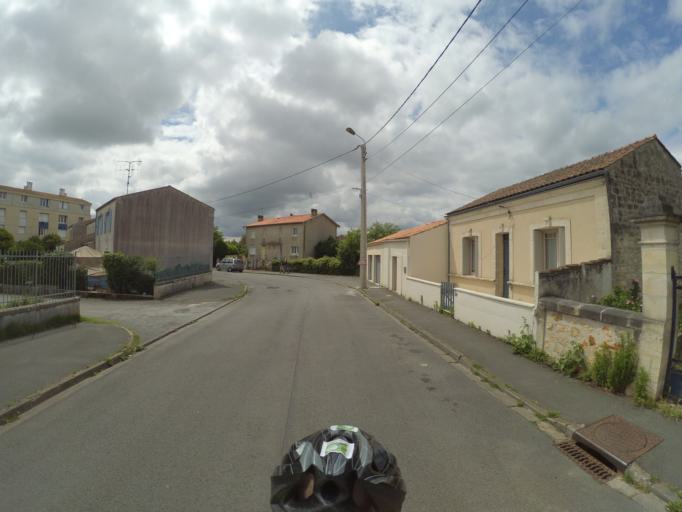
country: FR
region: Poitou-Charentes
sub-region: Departement de la Charente-Maritime
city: Rochefort
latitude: 45.9488
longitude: -0.9686
